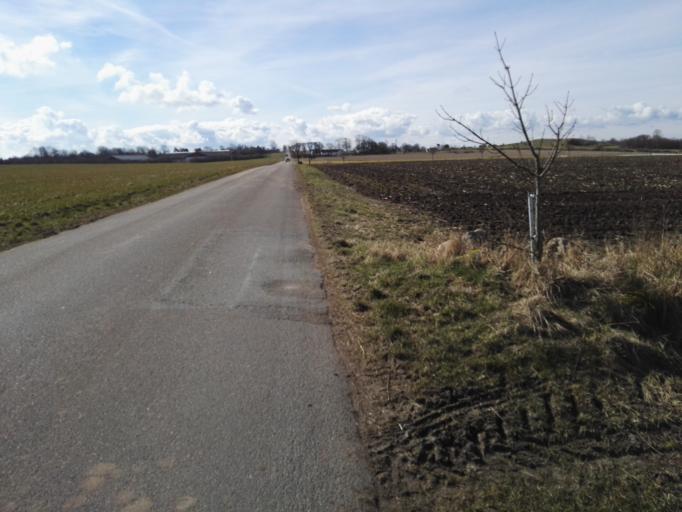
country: DK
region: Zealand
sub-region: Lejre Kommune
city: Ejby
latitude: 55.7735
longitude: 11.8197
